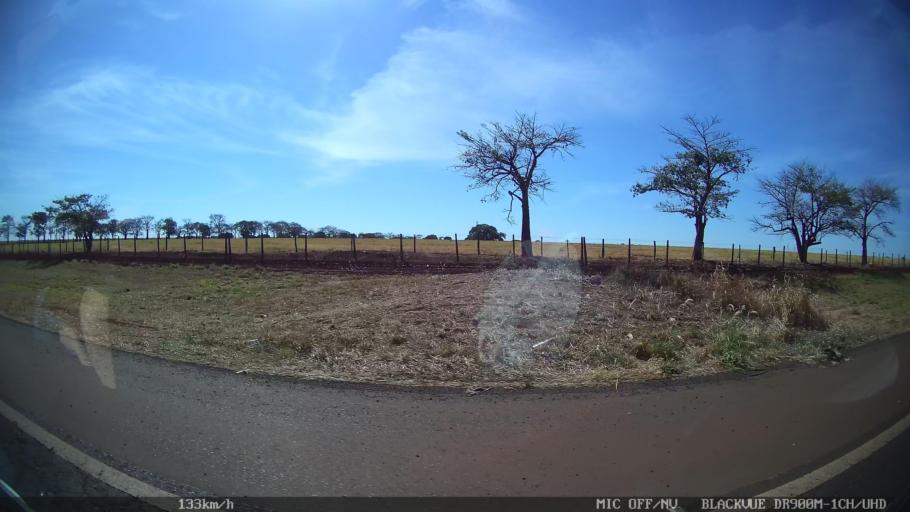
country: BR
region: Sao Paulo
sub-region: Ipua
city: Ipua
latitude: -20.4745
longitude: -48.0972
